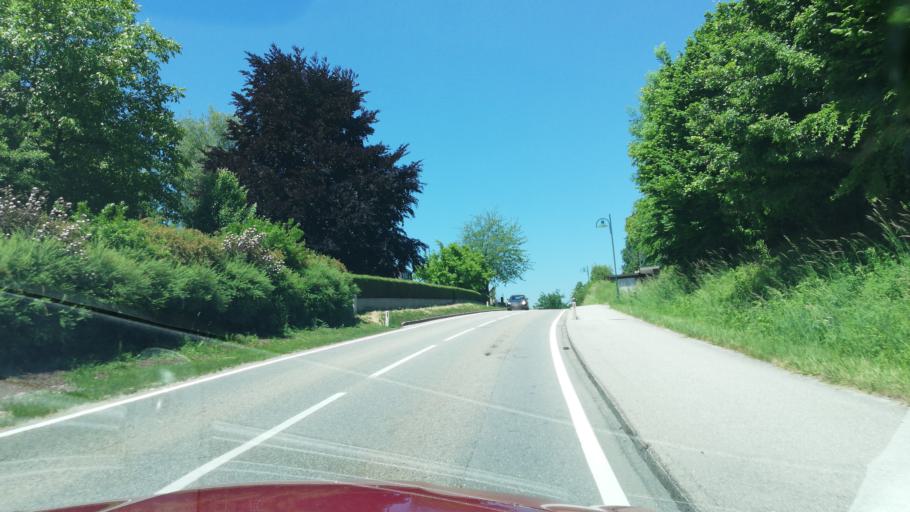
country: AT
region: Upper Austria
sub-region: Politischer Bezirk Vocklabruck
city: Oberndorf bei Schwanenstadt
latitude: 48.0640
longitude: 13.7657
